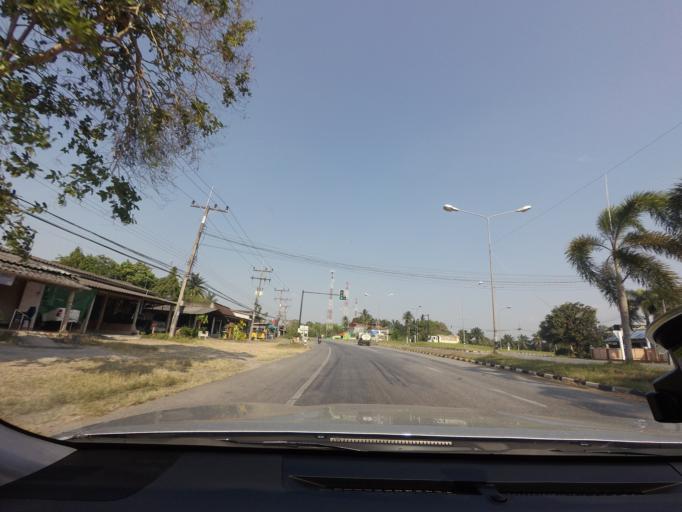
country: TH
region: Surat Thani
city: Chai Buri
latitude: 8.5681
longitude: 99.1158
